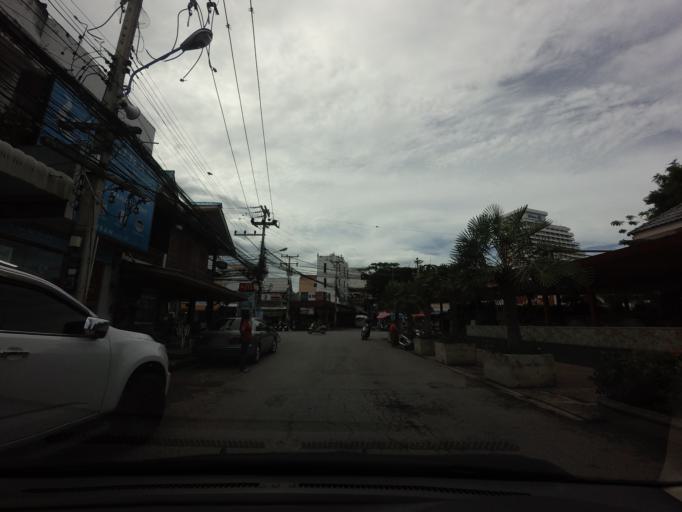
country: TH
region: Prachuap Khiri Khan
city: Hua Hin
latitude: 12.5686
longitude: 99.9598
